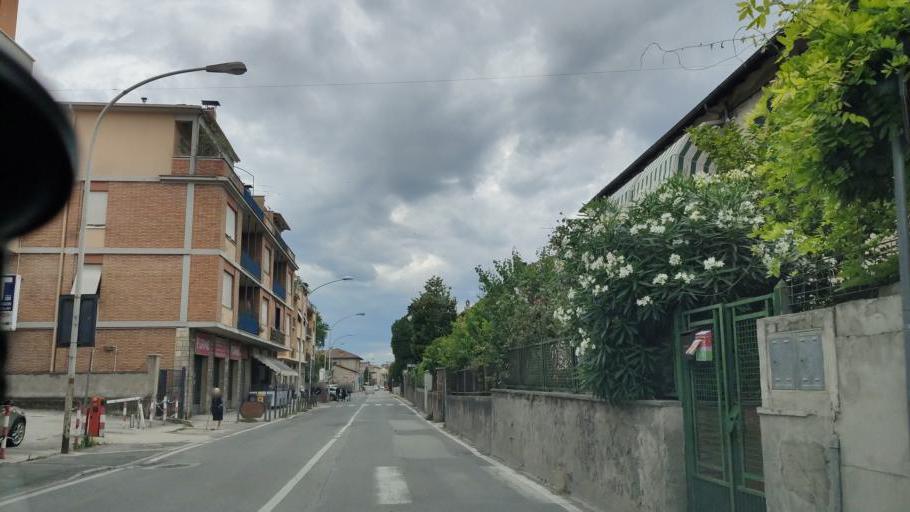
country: IT
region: Umbria
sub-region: Provincia di Terni
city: Terni
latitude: 42.5700
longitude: 12.6659
